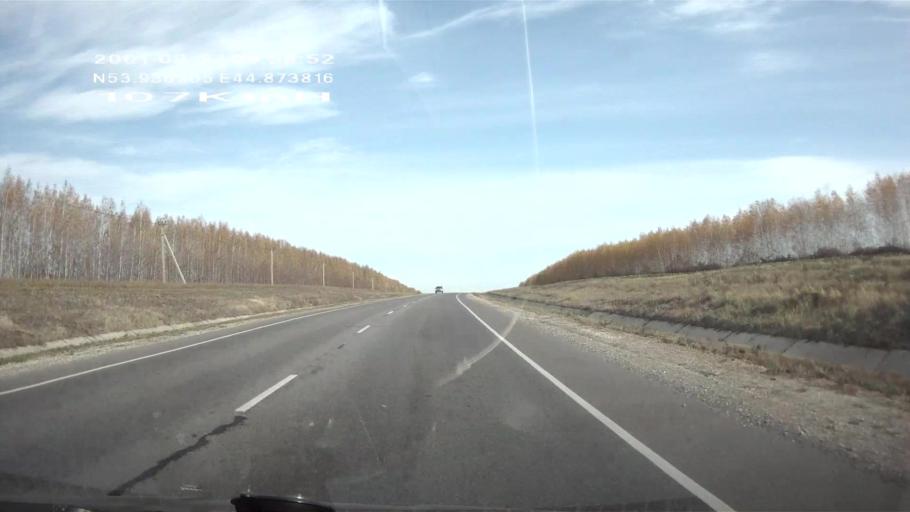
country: RU
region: Penza
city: Issa
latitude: 53.9374
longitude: 44.8742
